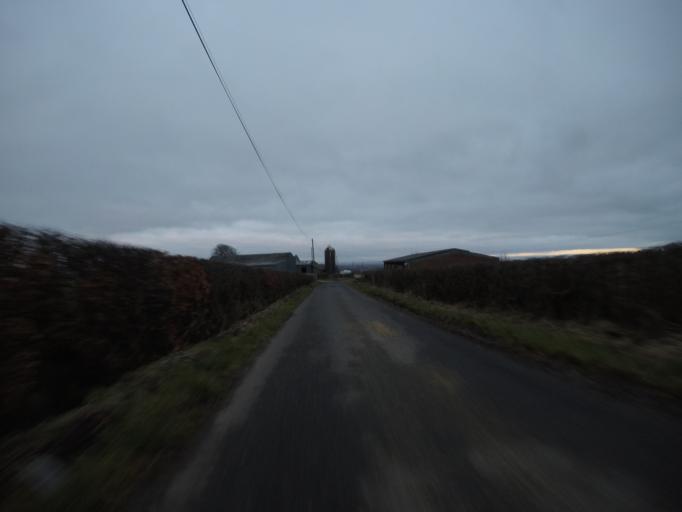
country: GB
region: Scotland
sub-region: North Ayrshire
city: Dalry
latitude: 55.6815
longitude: -4.7274
